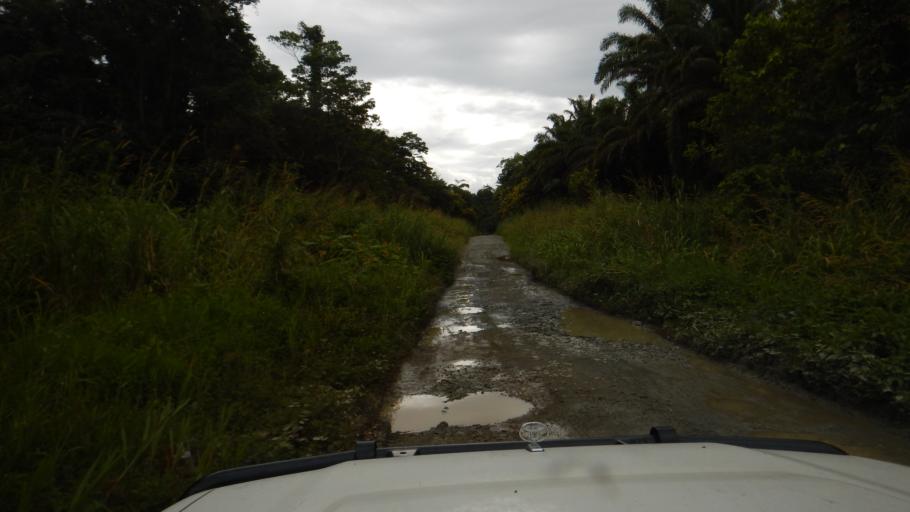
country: PG
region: Northern Province
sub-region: Sohe
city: Kokoda
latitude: -8.9168
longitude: 147.8591
